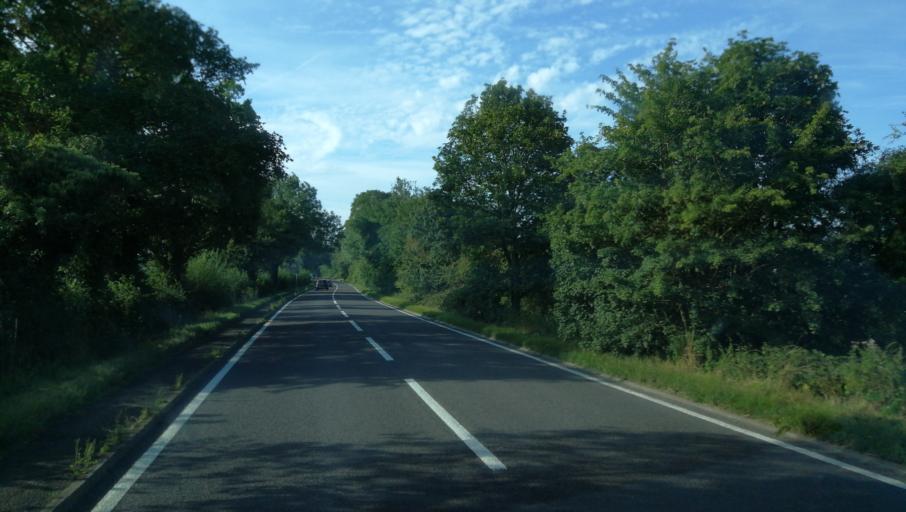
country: GB
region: England
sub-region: Oxfordshire
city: Deddington
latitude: 51.9274
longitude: -1.3250
